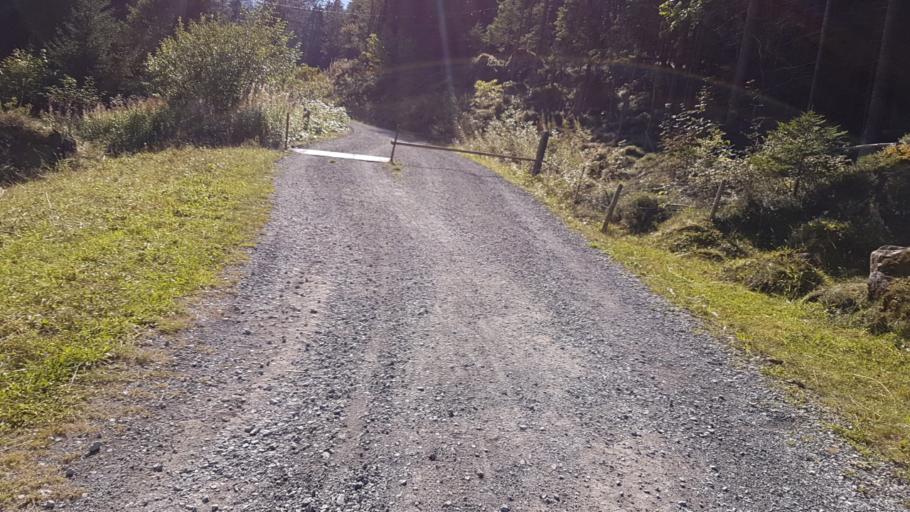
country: CH
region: Bern
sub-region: Frutigen-Niedersimmental District
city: Kandersteg
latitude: 46.5092
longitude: 7.6711
